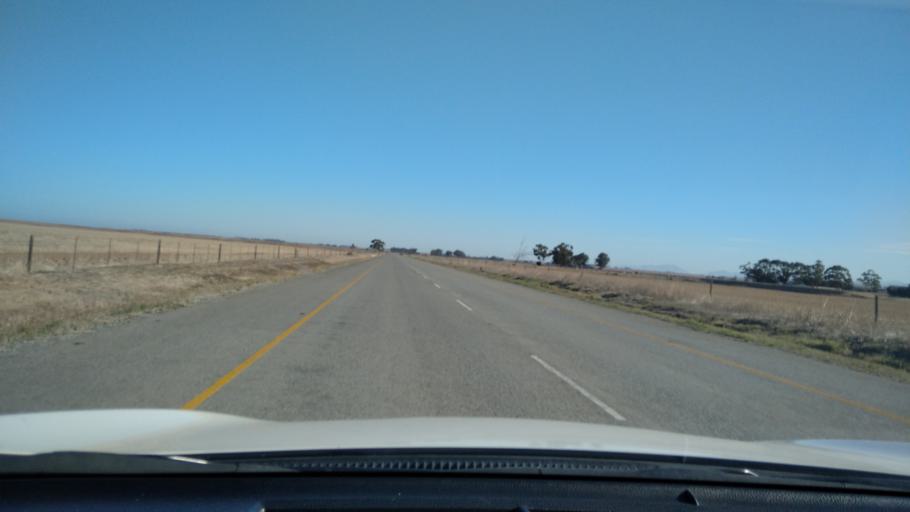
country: ZA
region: Western Cape
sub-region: West Coast District Municipality
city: Moorreesburg
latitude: -33.2906
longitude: 18.6085
